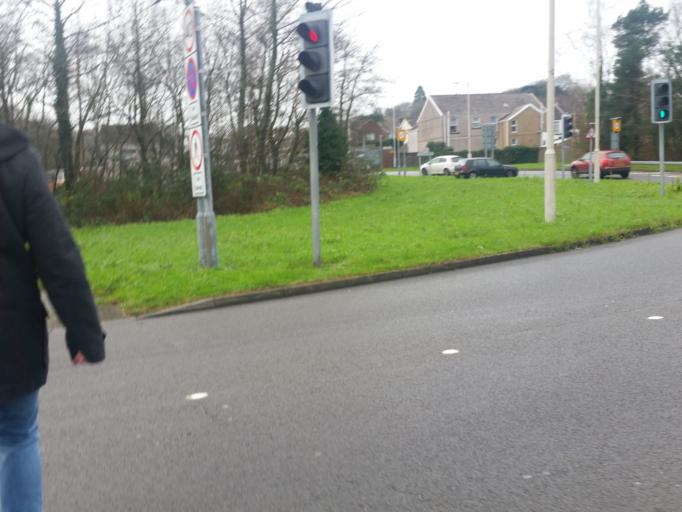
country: GB
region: Wales
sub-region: City and County of Swansea
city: Clydach
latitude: 51.6770
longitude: -3.9139
